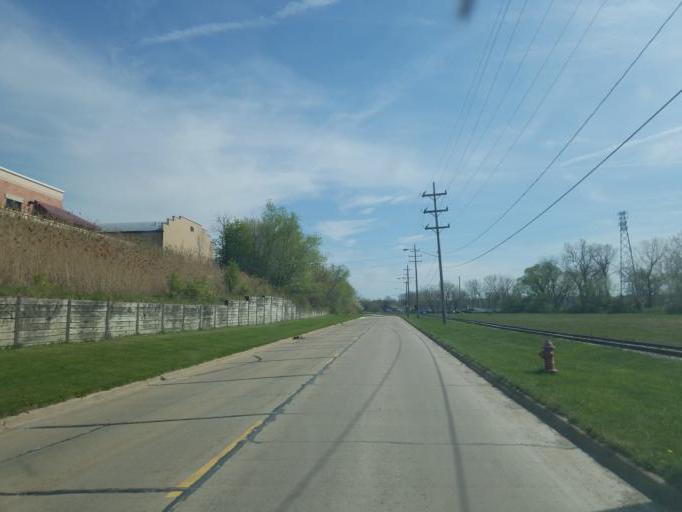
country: US
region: Ohio
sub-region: Lake County
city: Fairport Harbor
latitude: 41.7498
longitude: -81.2782
